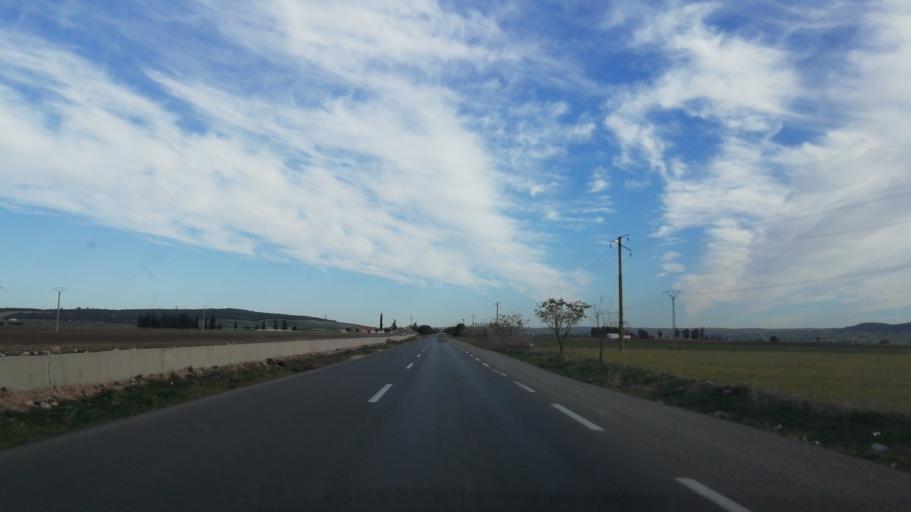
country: DZ
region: Sidi Bel Abbes
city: Sidi Bel Abbes
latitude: 35.1791
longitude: -0.4717
